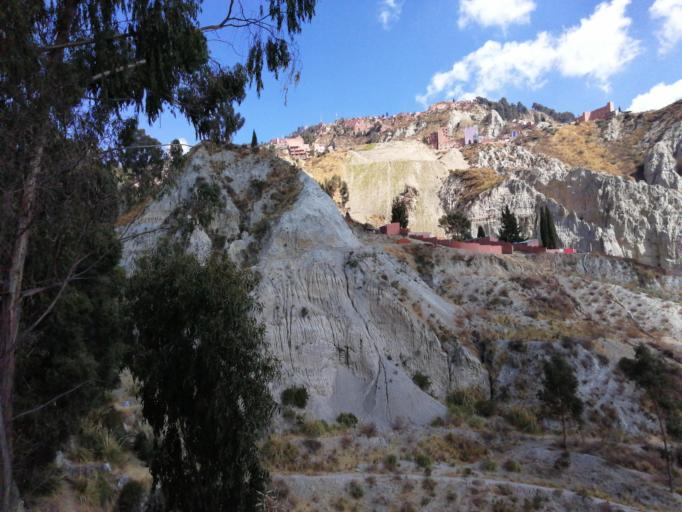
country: BO
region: La Paz
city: La Paz
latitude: -16.5314
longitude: -68.1338
